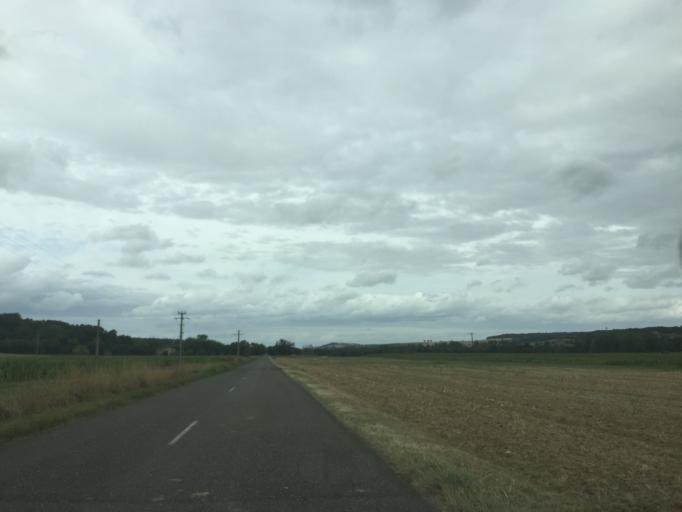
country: FR
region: Midi-Pyrenees
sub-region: Departement du Gers
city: Vic-Fezensac
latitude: 43.8012
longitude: 0.3869
